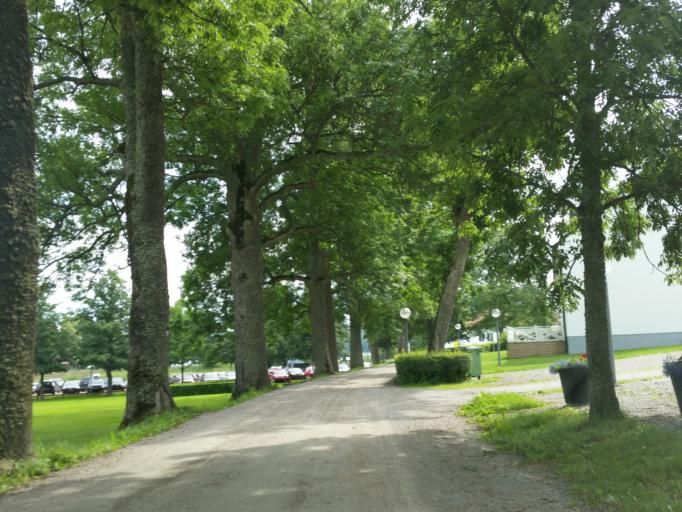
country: SE
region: Soedermanland
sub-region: Strangnas Kommun
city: Mariefred
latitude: 59.2577
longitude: 17.2129
